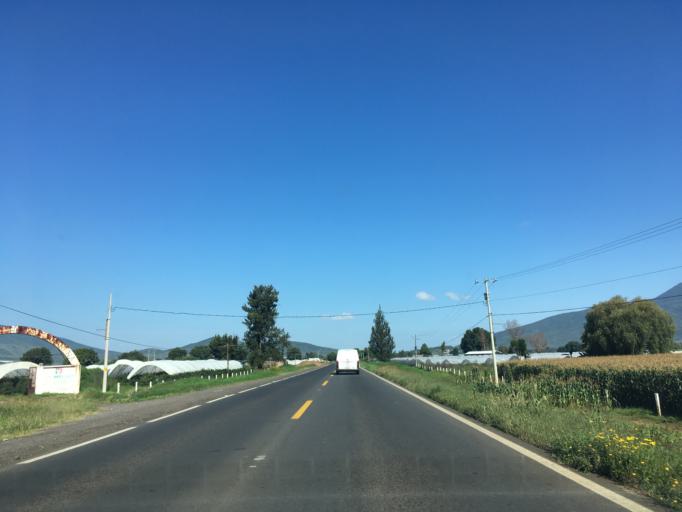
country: MX
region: Mexico
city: Tangancicuaro de Arista
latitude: 19.8652
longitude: -102.1904
